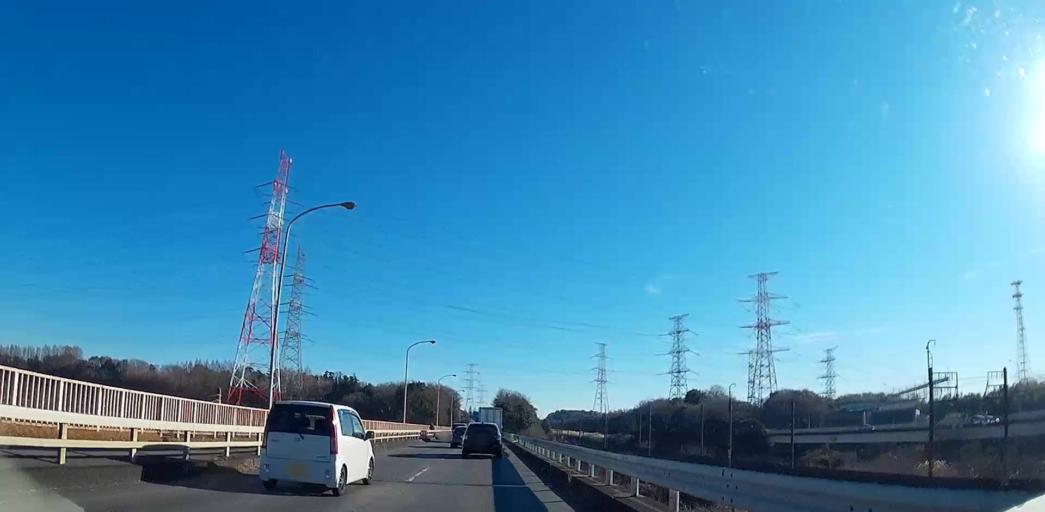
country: JP
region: Chiba
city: Shiroi
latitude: 35.7861
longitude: 140.0659
